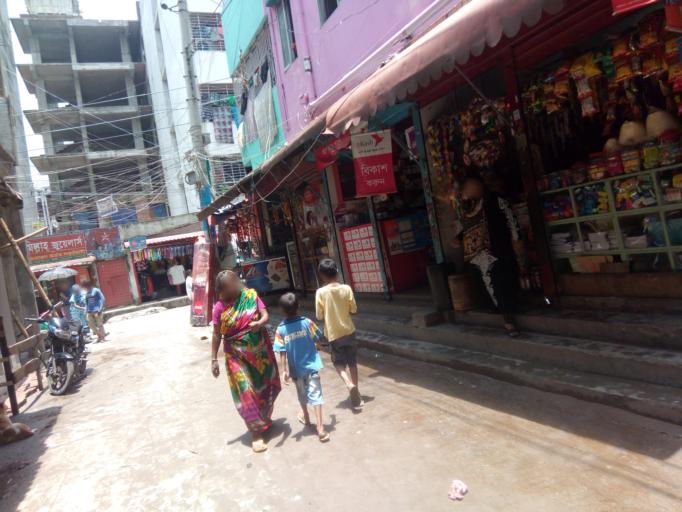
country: BD
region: Dhaka
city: Azimpur
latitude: 23.7668
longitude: 90.3615
